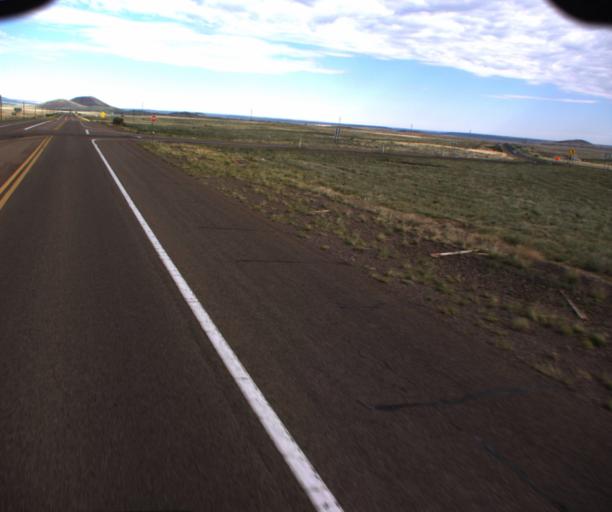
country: US
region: Arizona
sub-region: Apache County
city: Springerville
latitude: 34.1734
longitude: -109.3176
